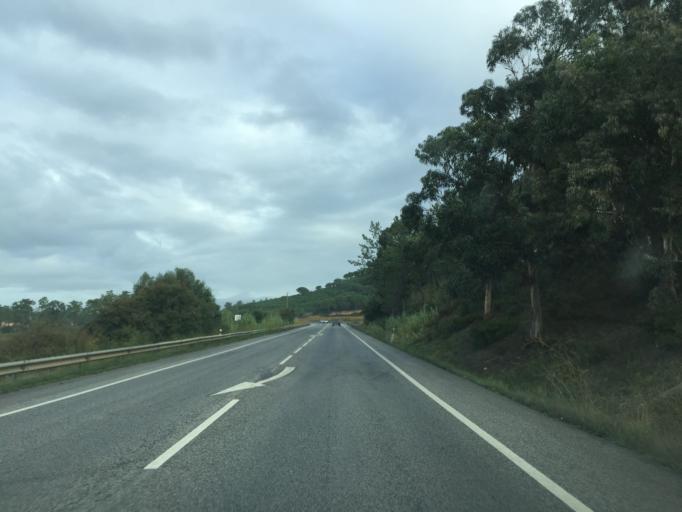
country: PT
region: Lisbon
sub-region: Azambuja
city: Alcoentre
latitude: 39.2129
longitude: -8.9542
